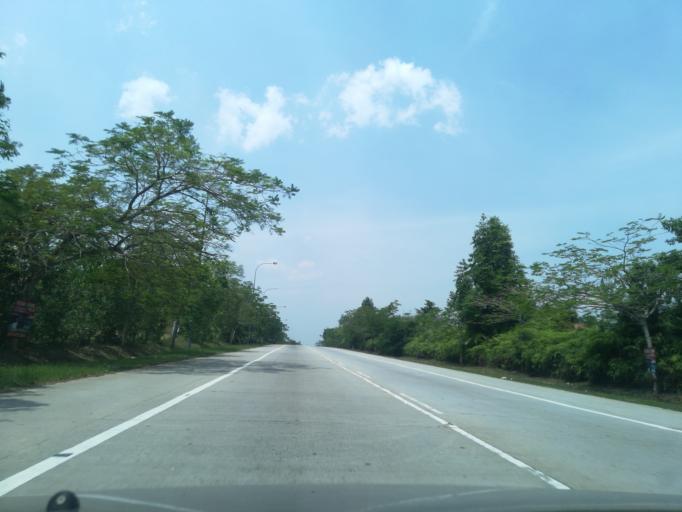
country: MY
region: Kedah
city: Kulim
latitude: 5.4186
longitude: 100.5668
